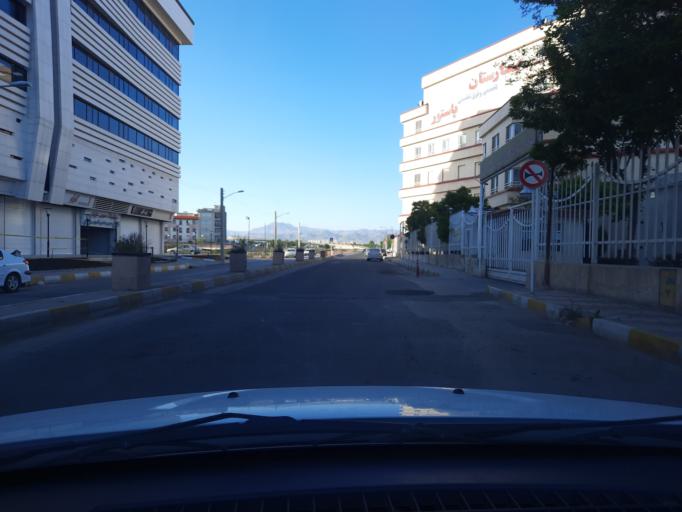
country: IR
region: Qazvin
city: Qazvin
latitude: 36.2663
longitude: 50.0244
